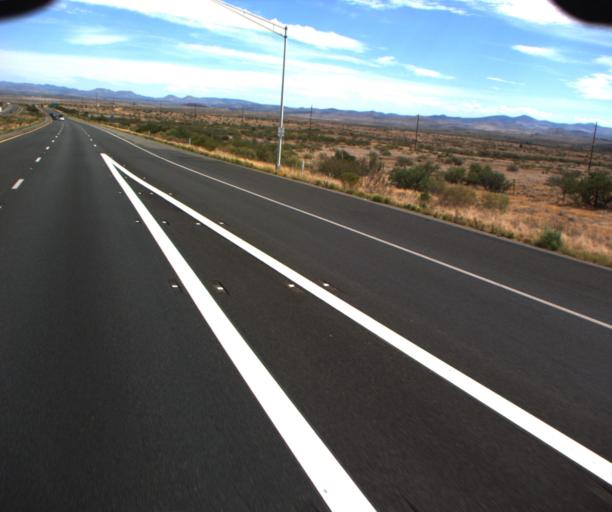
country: US
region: Arizona
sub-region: Yavapai County
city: Cordes Lakes
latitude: 34.3379
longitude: -112.1187
